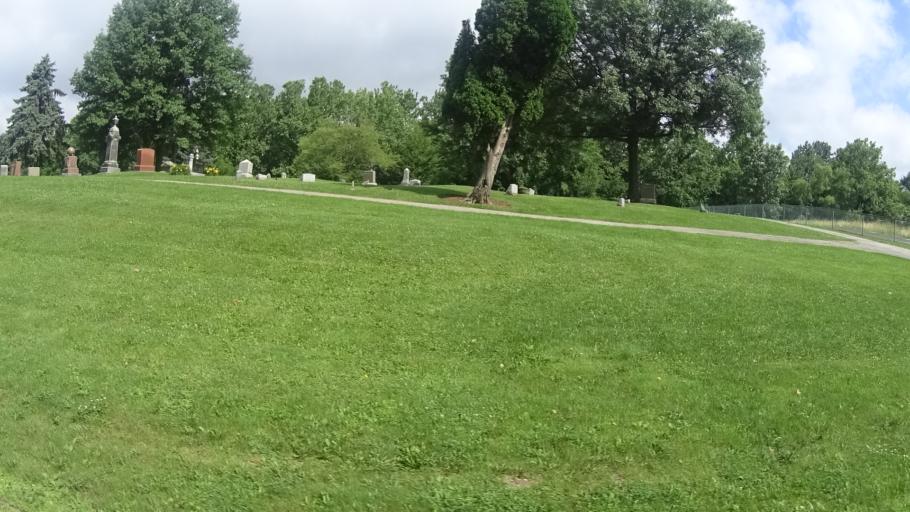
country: US
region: Ohio
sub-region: Huron County
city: Wakeman
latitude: 41.3204
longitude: -82.4227
